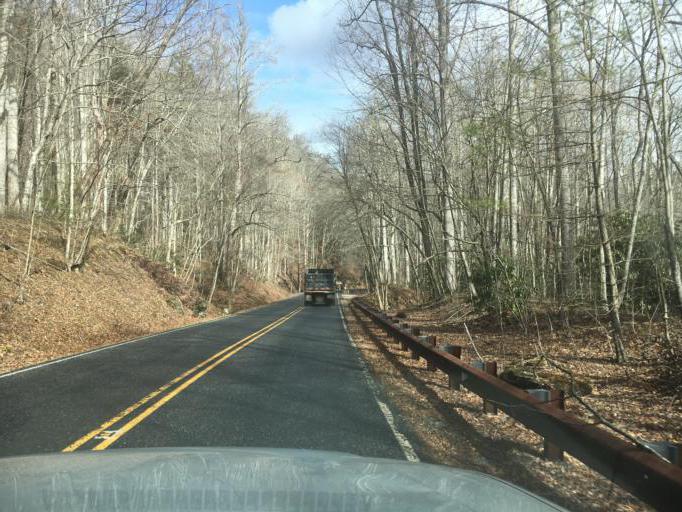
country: US
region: North Carolina
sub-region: Transylvania County
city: Brevard
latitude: 35.3721
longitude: -82.8162
